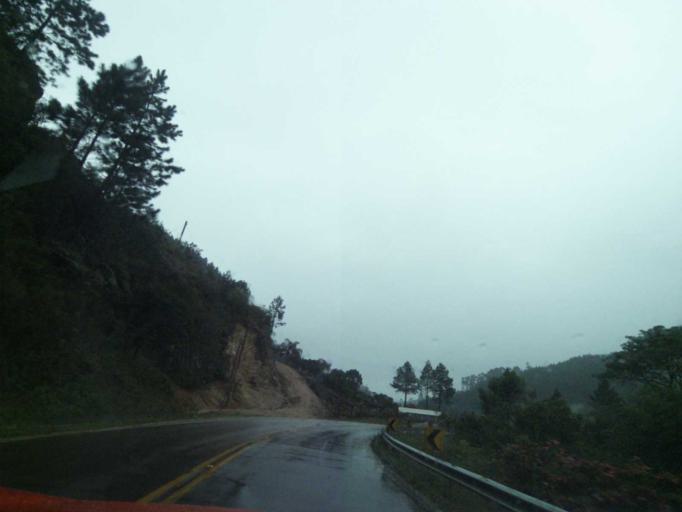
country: BR
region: Santa Catarina
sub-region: Anitapolis
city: Anitapolis
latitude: -27.8334
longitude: -49.0518
